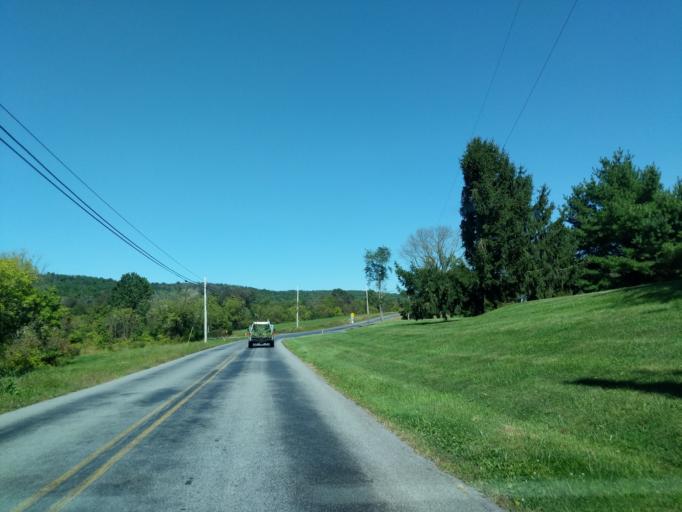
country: US
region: Pennsylvania
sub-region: Montgomery County
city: East Greenville
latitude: 40.4219
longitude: -75.5025
